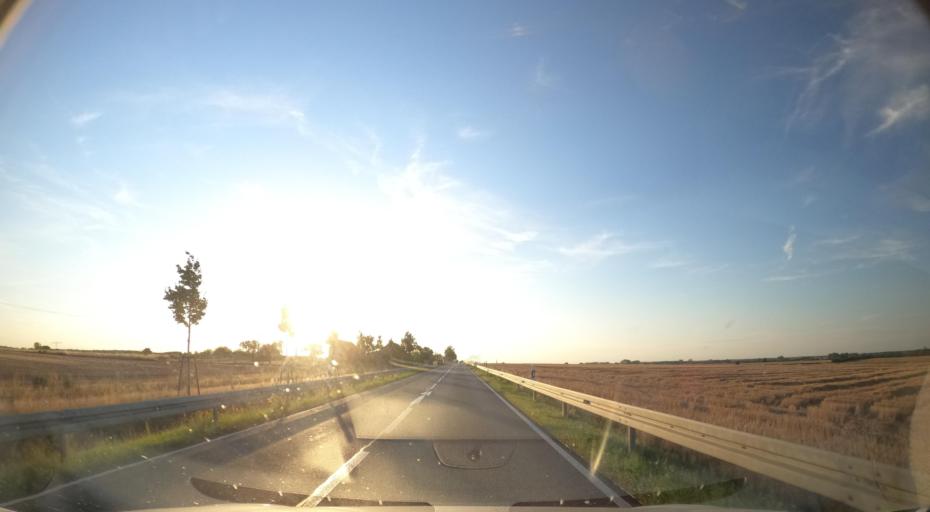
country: DE
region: Brandenburg
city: Brussow
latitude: 53.4815
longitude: 14.1118
